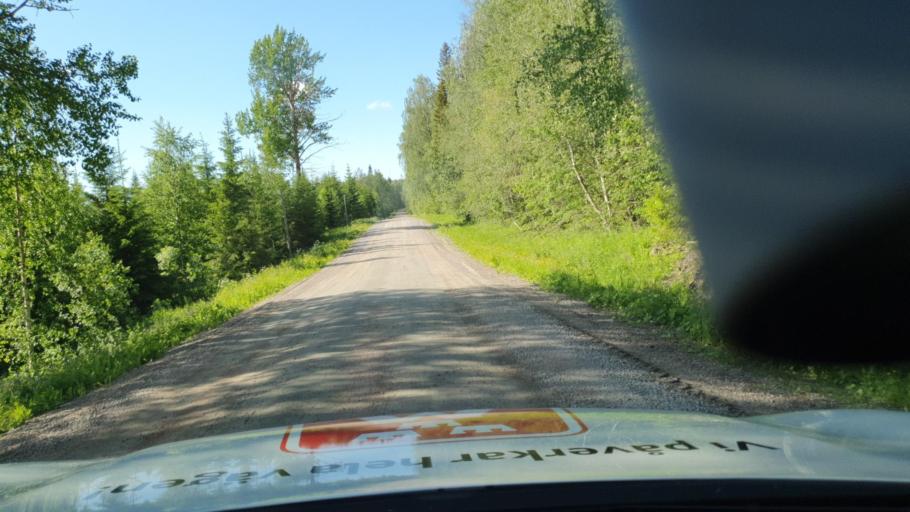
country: SE
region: Vaesterbotten
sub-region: Vannas Kommun
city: Vaennaes
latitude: 63.7823
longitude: 19.6318
